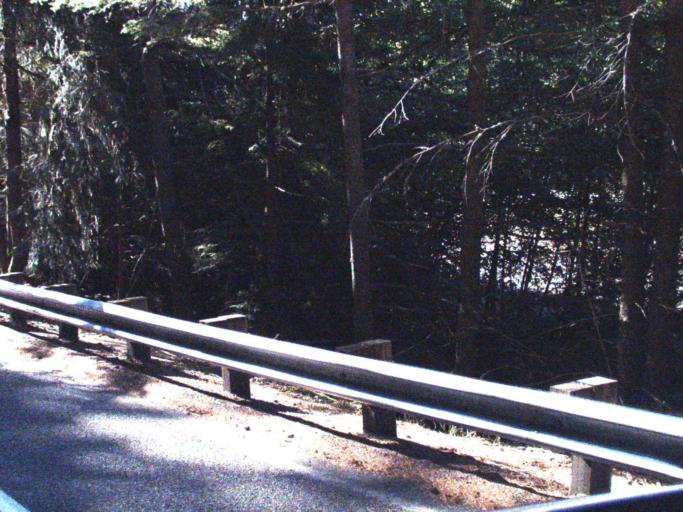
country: US
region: Washington
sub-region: King County
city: Enumclaw
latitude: 47.1648
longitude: -121.7426
